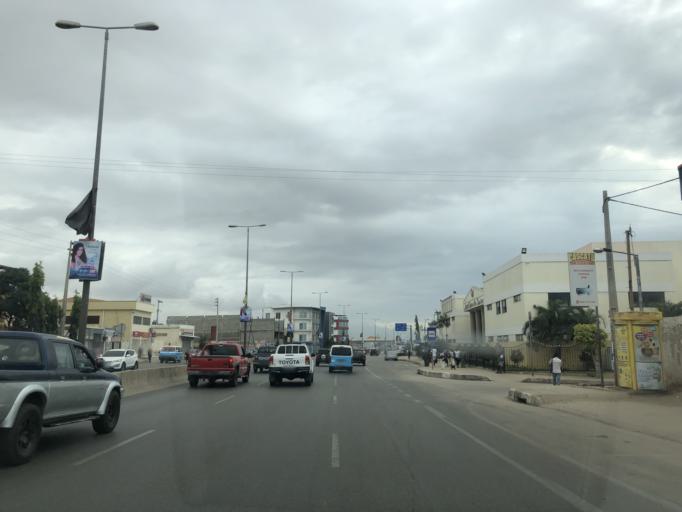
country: AO
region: Luanda
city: Luanda
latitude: -8.8877
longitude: 13.2049
